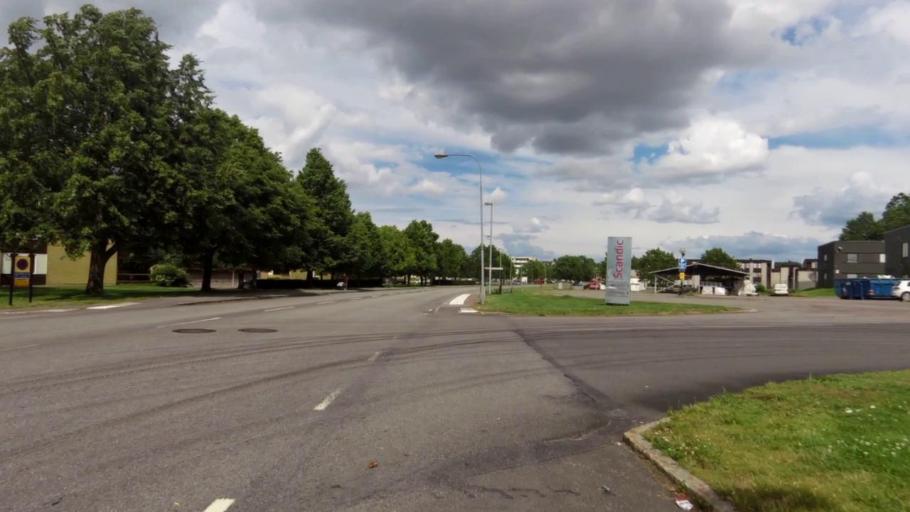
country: SE
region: OEstergoetland
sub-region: Linkopings Kommun
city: Malmslatt
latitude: 58.4063
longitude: 15.5594
